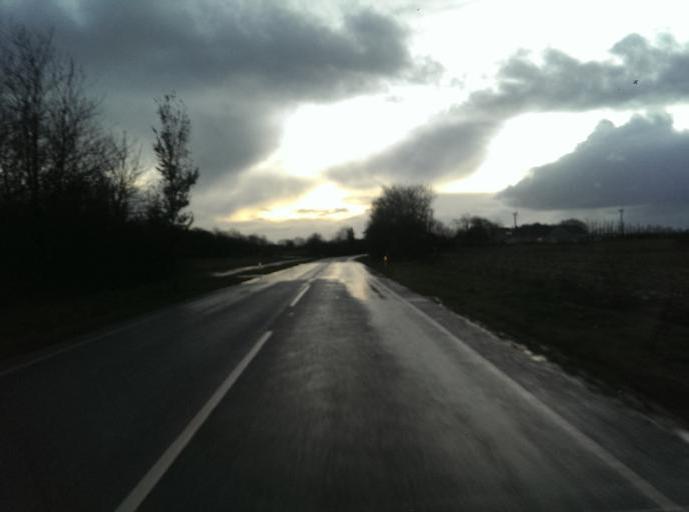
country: DK
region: South Denmark
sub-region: Esbjerg Kommune
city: Bramming
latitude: 55.4607
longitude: 8.6926
